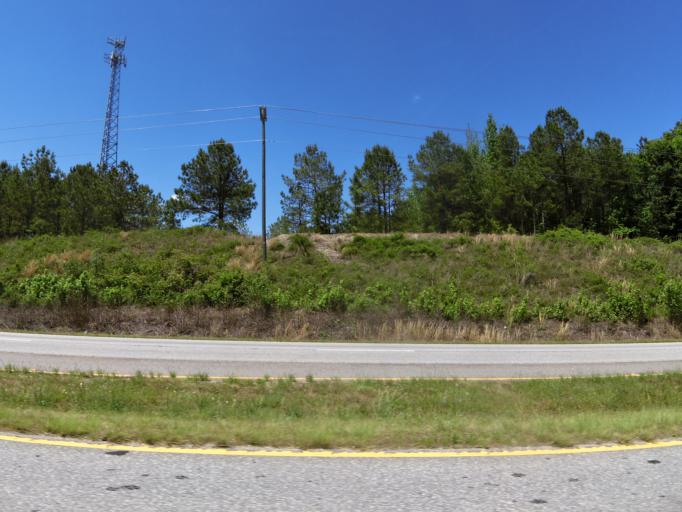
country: US
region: South Carolina
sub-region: Aiken County
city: Clearwater
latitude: 33.5085
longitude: -81.8788
